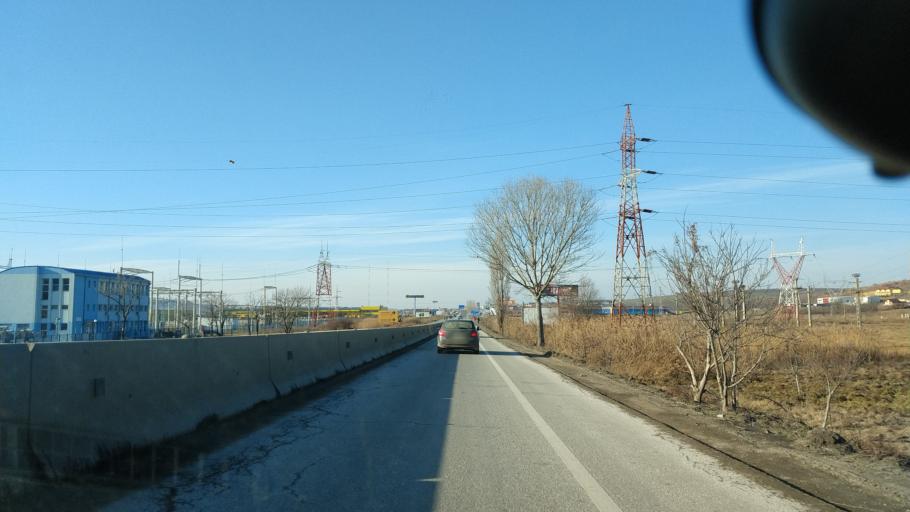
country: RO
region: Iasi
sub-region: Comuna Valea Lupului
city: Valea Lupului
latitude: 47.1786
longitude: 27.4835
